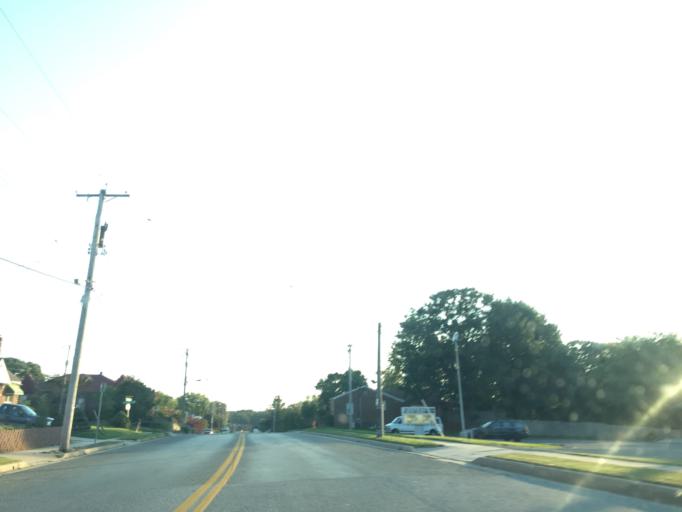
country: US
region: Maryland
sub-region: Baltimore County
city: Essex
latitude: 39.3214
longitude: -76.4633
